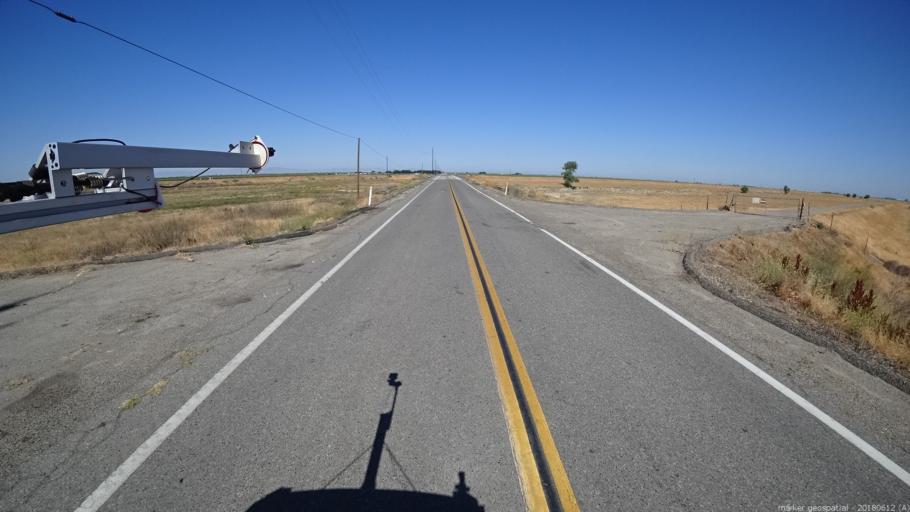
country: US
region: California
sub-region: Fresno County
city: Firebaugh
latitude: 37.0182
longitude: -120.4325
